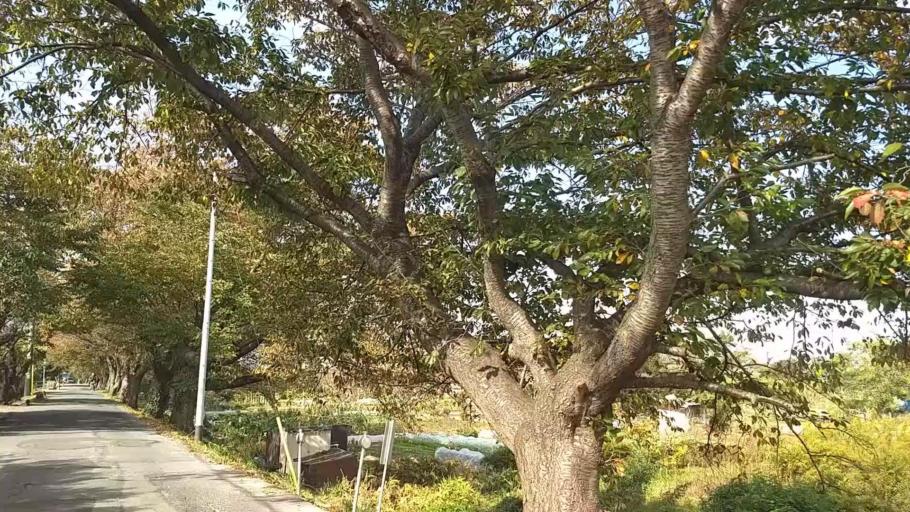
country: JP
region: Kanagawa
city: Atsugi
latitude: 35.4495
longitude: 139.3654
